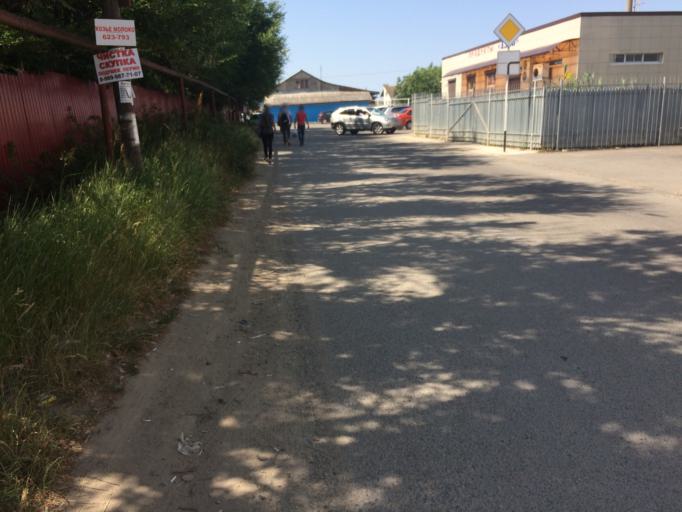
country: RU
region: Stavropol'skiy
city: Tatarka
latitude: 44.9891
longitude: 41.9371
